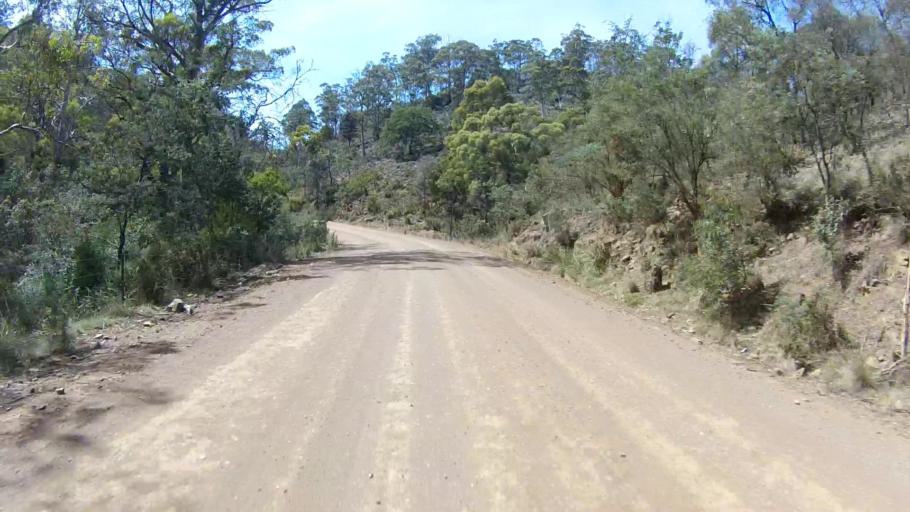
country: AU
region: Tasmania
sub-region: Sorell
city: Sorell
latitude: -42.6409
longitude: 147.7330
